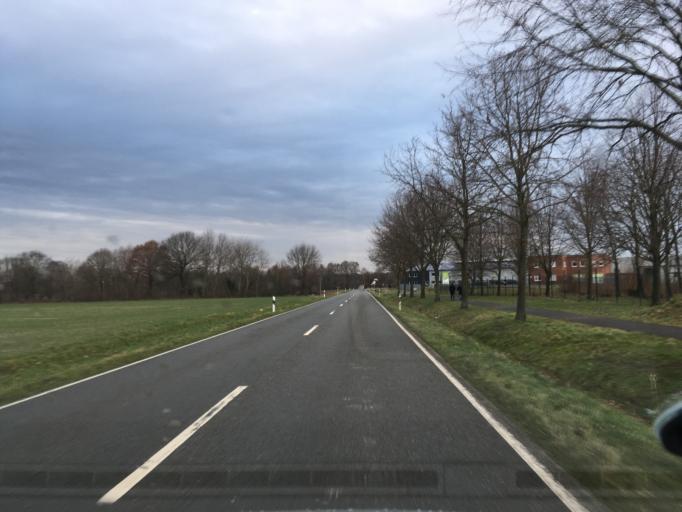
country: DE
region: North Rhine-Westphalia
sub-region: Regierungsbezirk Munster
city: Schoppingen
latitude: 52.1008
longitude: 7.2269
